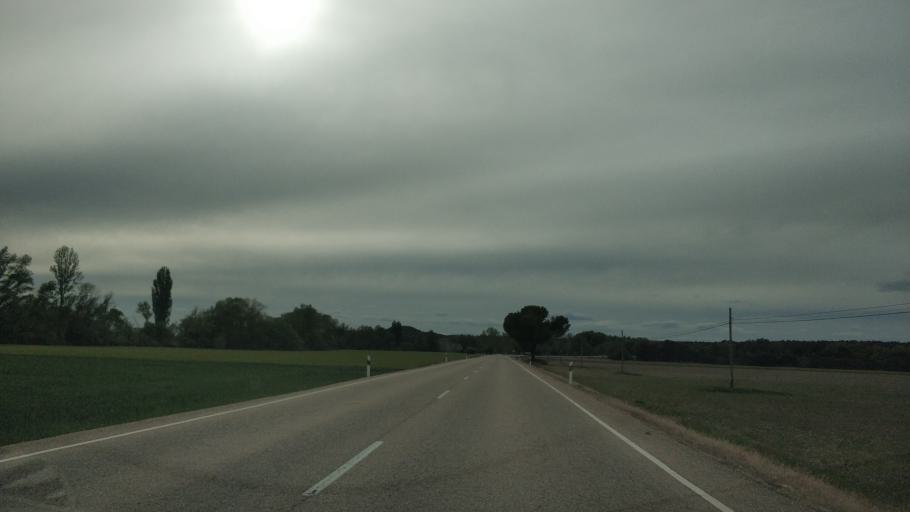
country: ES
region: Castille and Leon
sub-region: Provincia de Soria
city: Bayubas de Abajo
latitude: 41.4993
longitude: -2.8819
